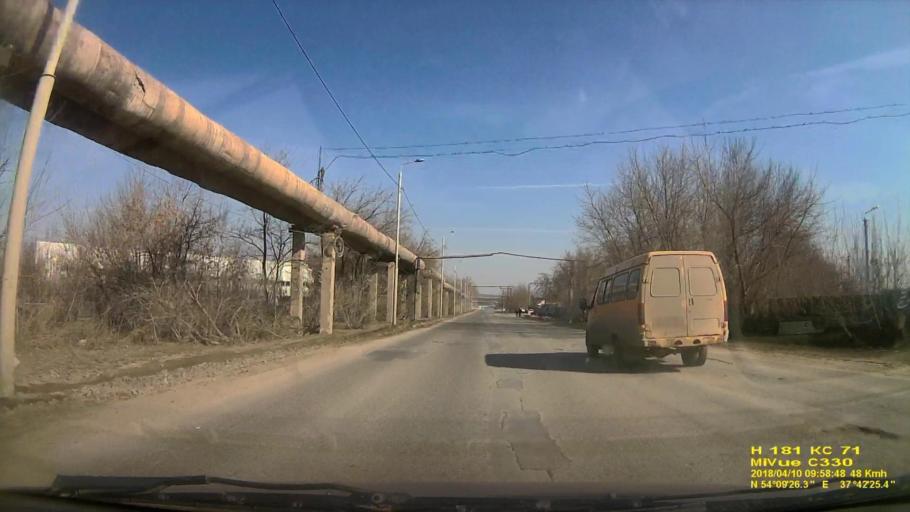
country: RU
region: Tula
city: Tula
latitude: 54.1575
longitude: 37.7071
